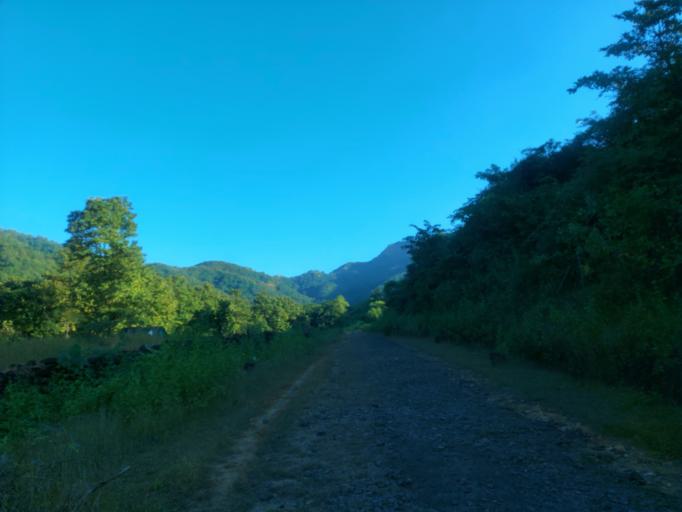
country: IN
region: Maharashtra
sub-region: Sindhudurg
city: Kudal
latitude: 16.0749
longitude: 73.8259
